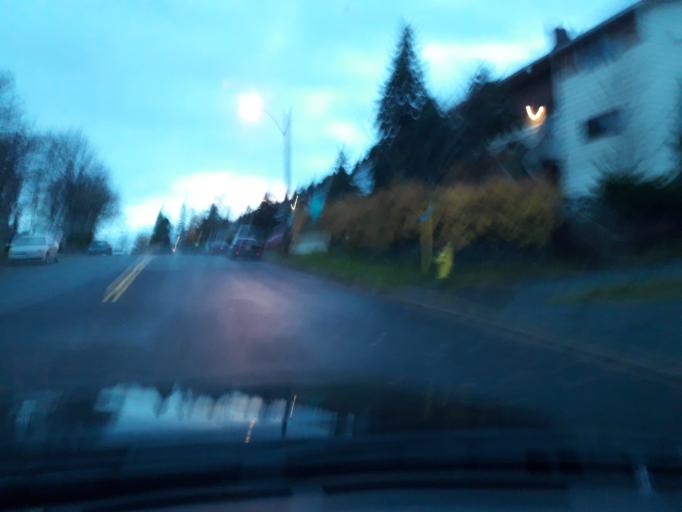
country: CA
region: Newfoundland and Labrador
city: St. John's
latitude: 47.5682
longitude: -52.7500
